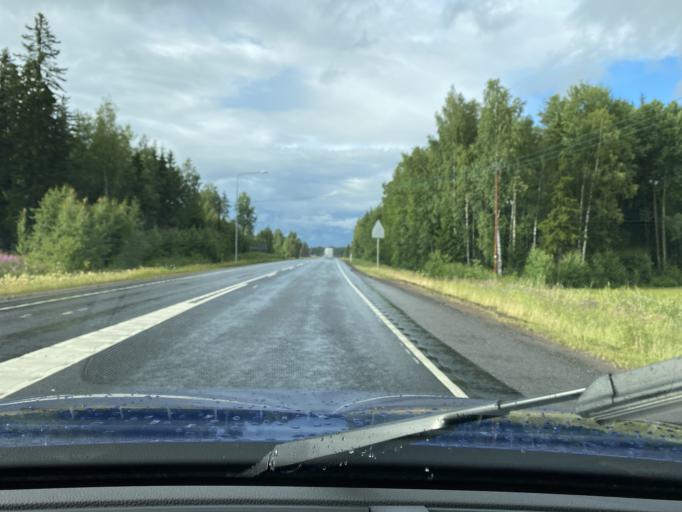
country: FI
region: Uusimaa
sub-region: Helsinki
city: Nurmijaervi
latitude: 60.4751
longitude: 24.8430
